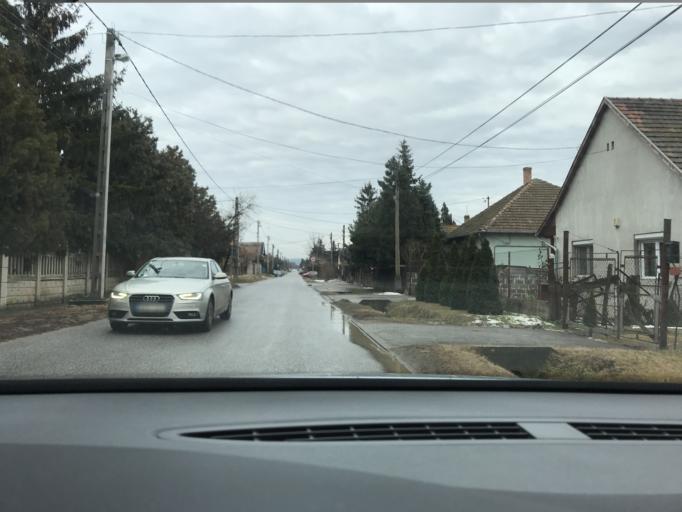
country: HU
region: Pest
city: Fot
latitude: 47.6279
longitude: 19.1719
